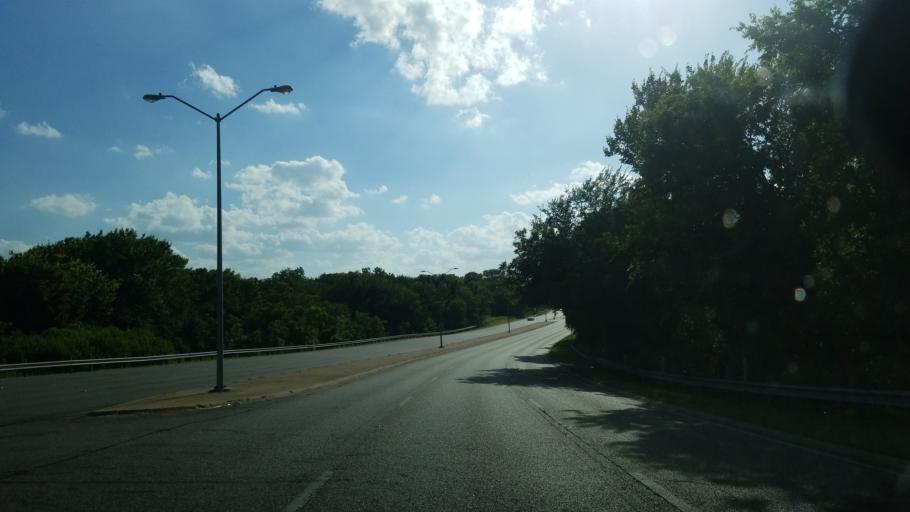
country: US
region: Texas
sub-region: Dallas County
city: Balch Springs
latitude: 32.7633
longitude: -96.7045
